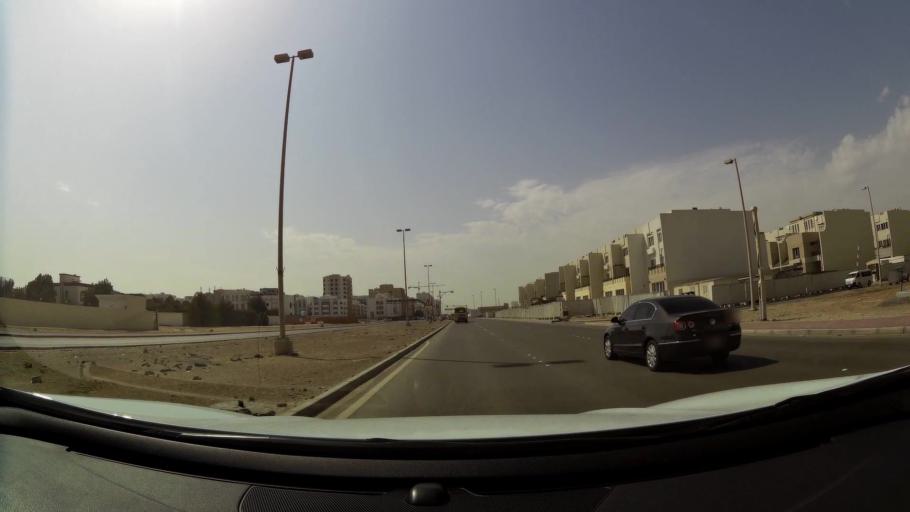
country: AE
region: Abu Dhabi
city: Abu Dhabi
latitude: 24.3384
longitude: 54.5408
